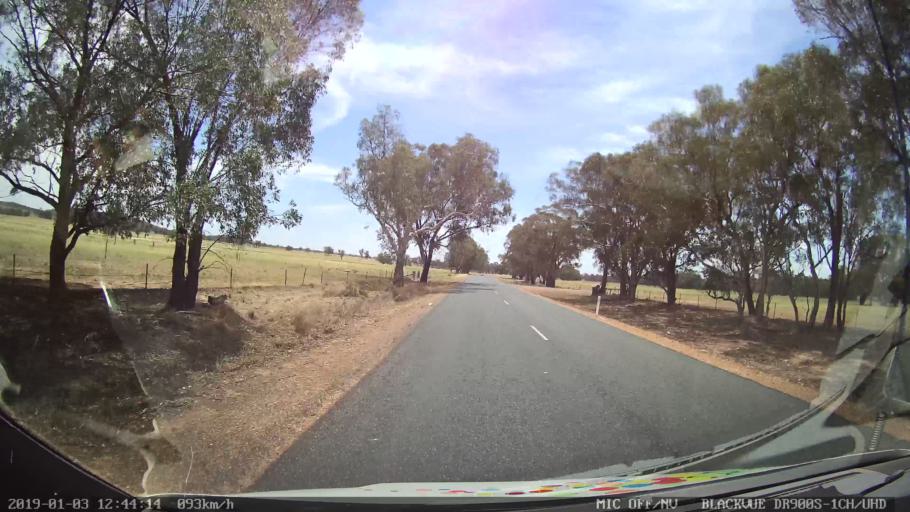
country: AU
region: New South Wales
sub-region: Weddin
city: Grenfell
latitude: -33.7643
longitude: 148.2150
